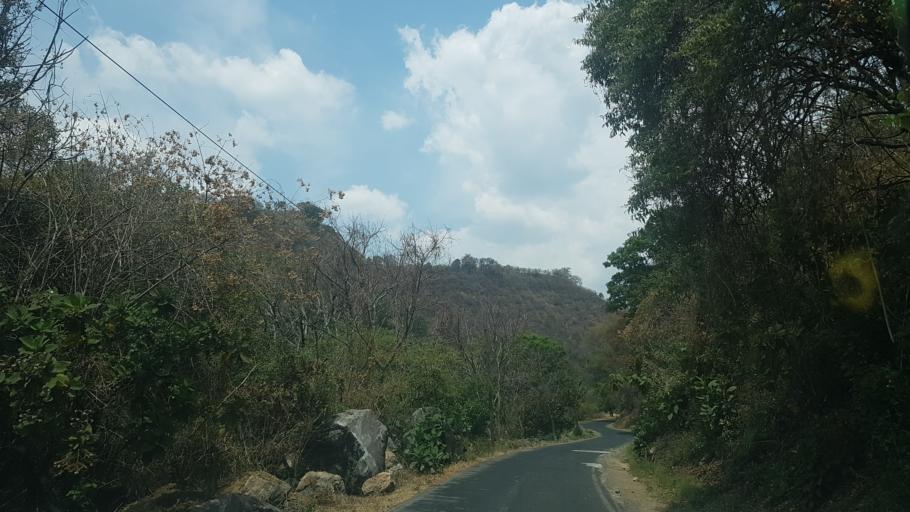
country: MX
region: Puebla
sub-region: Tochimilco
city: La Magdalena Yancuitlalpan
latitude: 18.8721
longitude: -98.6086
